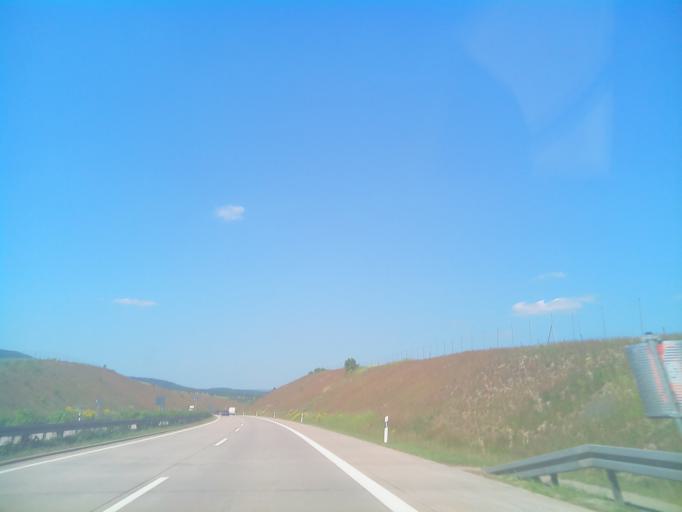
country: DE
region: Thuringia
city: Rohr
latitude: 50.5860
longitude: 10.4892
